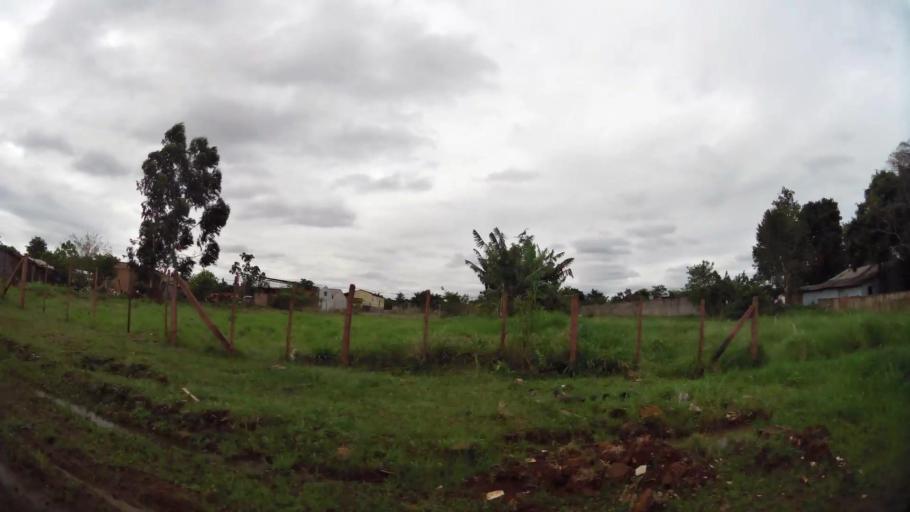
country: PY
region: Alto Parana
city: Ciudad del Este
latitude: -25.4040
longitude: -54.6366
